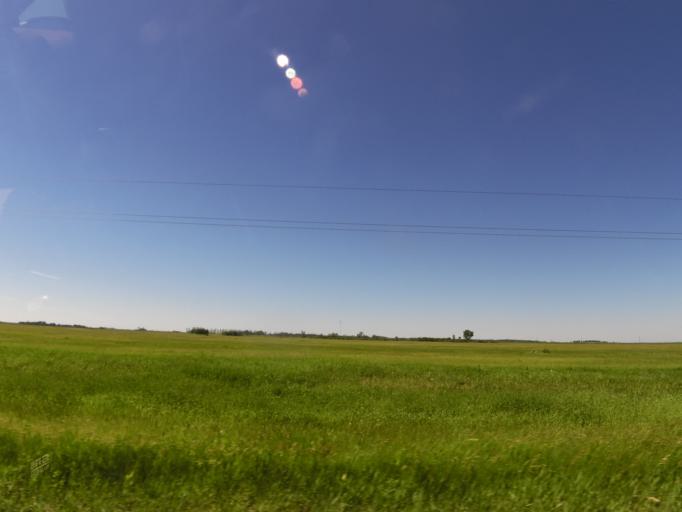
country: US
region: Minnesota
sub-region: Red Lake County
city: Red Lake Falls
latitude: 47.7572
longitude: -96.2596
